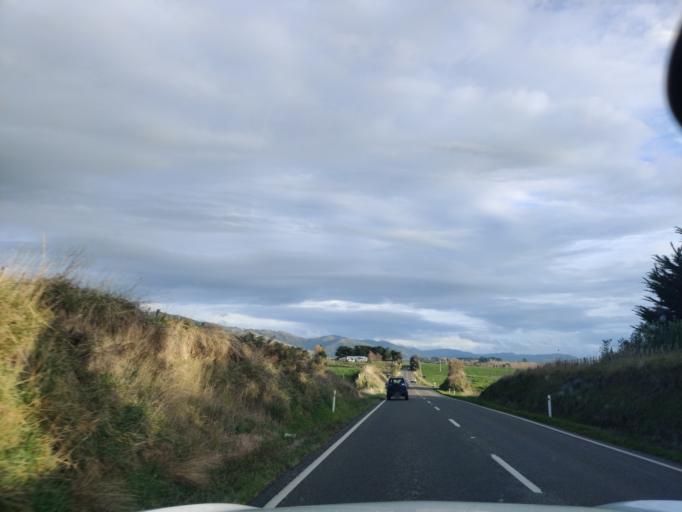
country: NZ
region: Manawatu-Wanganui
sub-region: Palmerston North City
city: Palmerston North
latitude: -40.5011
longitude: 175.4879
